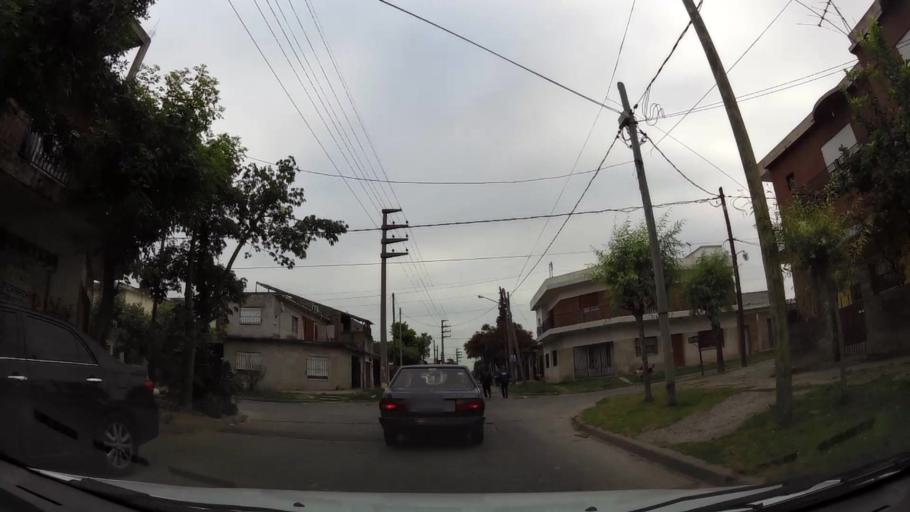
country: AR
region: Buenos Aires
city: San Justo
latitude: -34.7038
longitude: -58.5693
